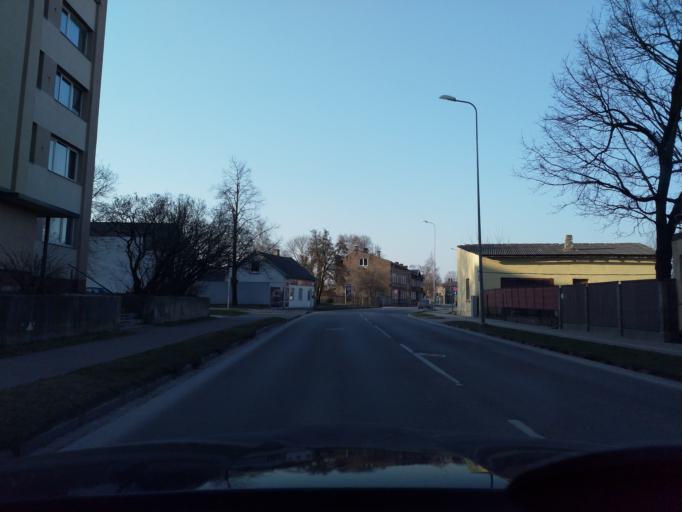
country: LV
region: Liepaja
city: Liepaja
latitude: 56.5019
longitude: 21.0185
